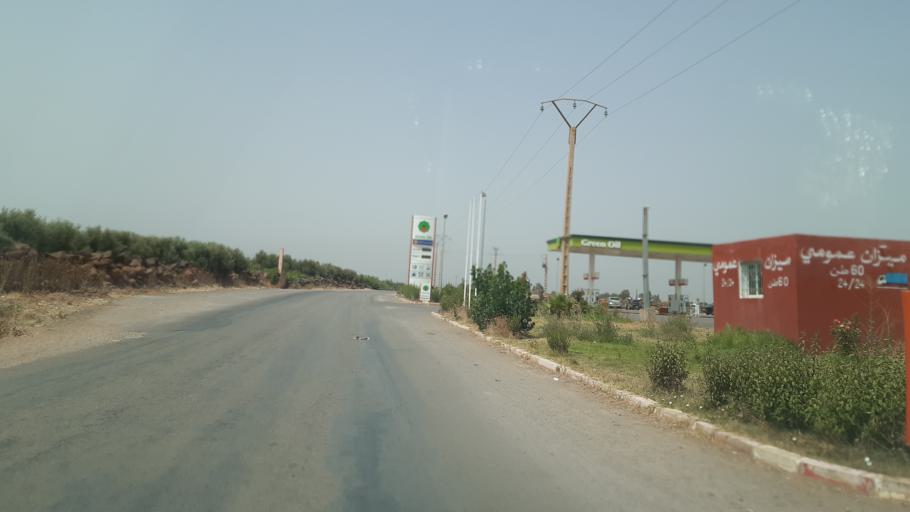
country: MA
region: Fes-Boulemane
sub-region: Fes
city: Oulad Tayeb
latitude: 33.8394
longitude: -5.1309
